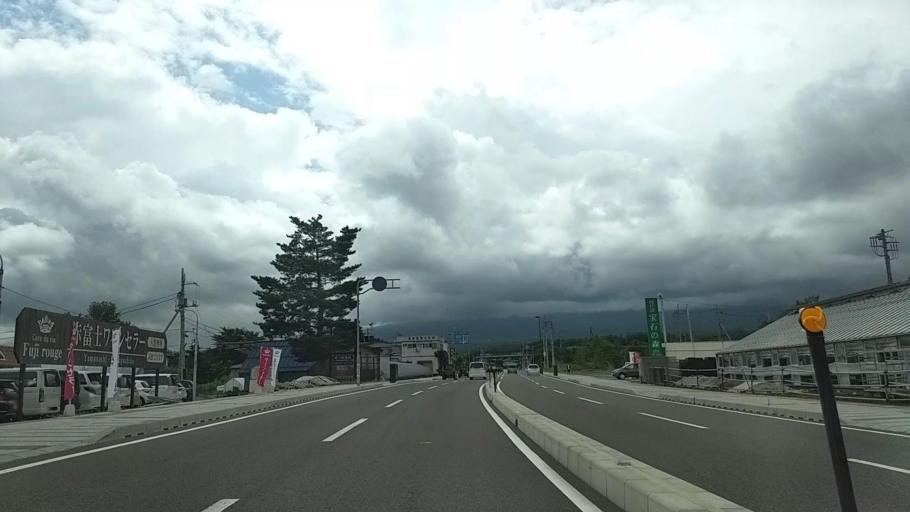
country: JP
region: Yamanashi
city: Fujikawaguchiko
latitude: 35.4939
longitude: 138.7566
